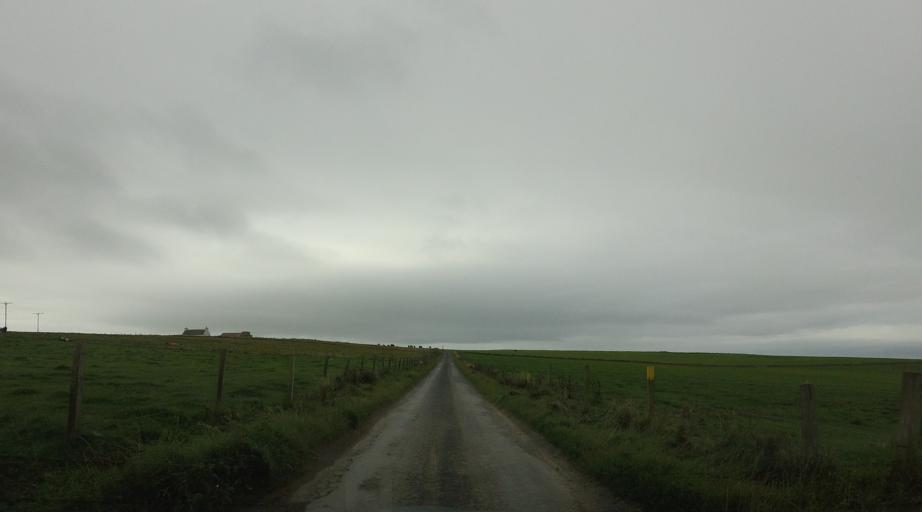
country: GB
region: Scotland
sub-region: Orkney Islands
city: Orkney
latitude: 58.8005
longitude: -2.9472
